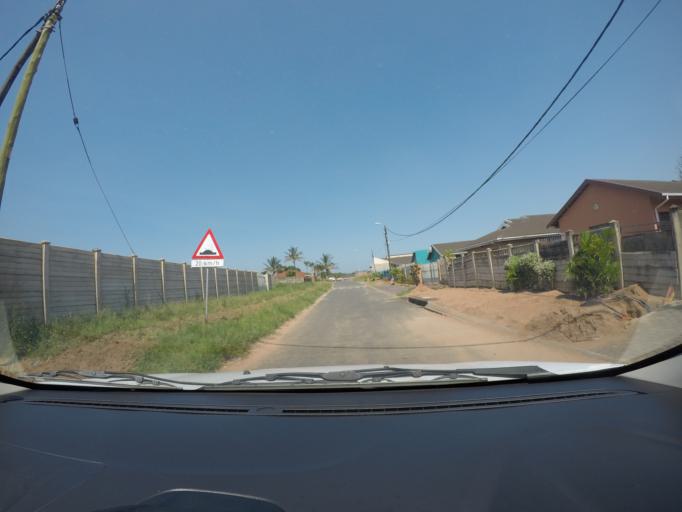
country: ZA
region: KwaZulu-Natal
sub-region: uThungulu District Municipality
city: Richards Bay
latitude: -28.7267
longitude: 32.0385
